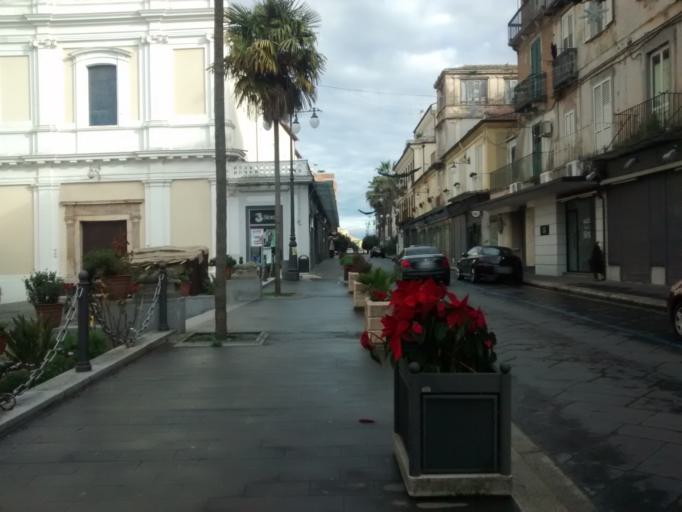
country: IT
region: Calabria
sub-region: Provincia di Vibo-Valentia
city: Vibo Valentia
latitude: 38.6728
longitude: 16.1049
